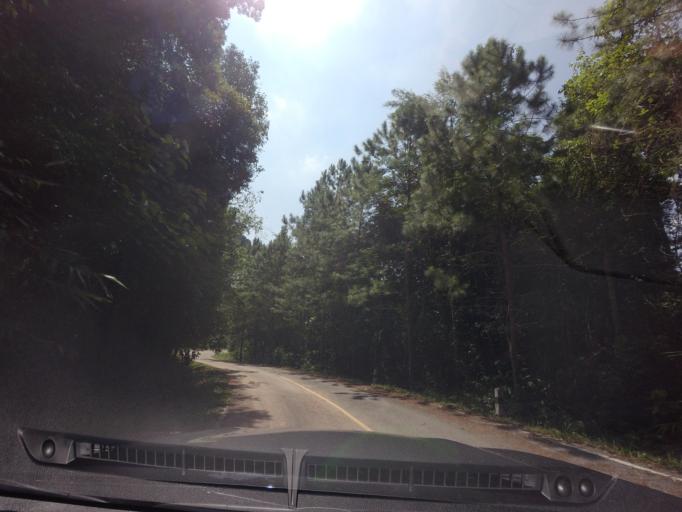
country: TH
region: Loei
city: Na Haeo
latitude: 17.5094
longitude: 100.9413
